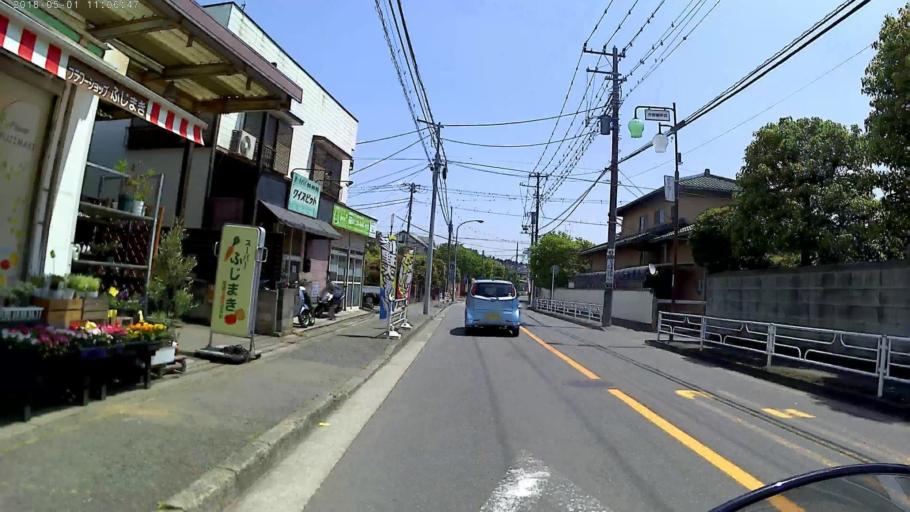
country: JP
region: Kanagawa
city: Minami-rinkan
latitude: 35.4827
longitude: 139.5320
